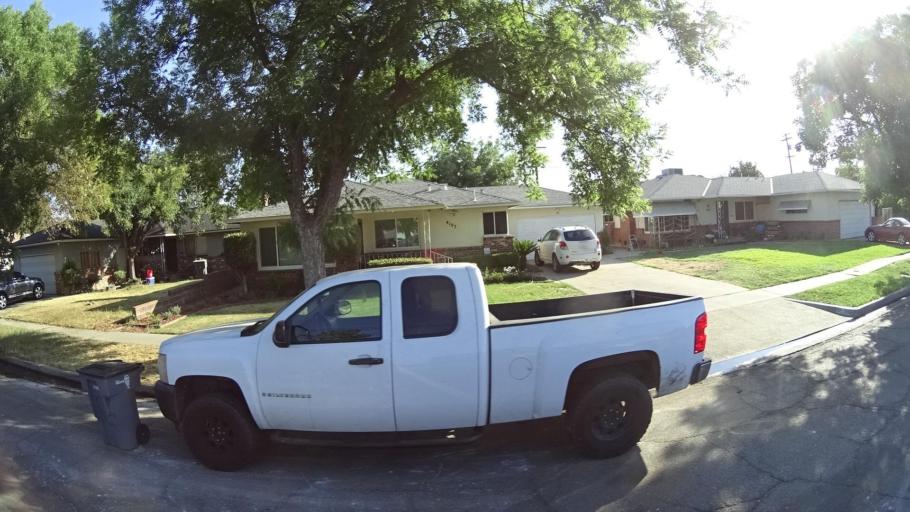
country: US
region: California
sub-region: Fresno County
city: Fresno
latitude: 36.7775
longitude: -119.7566
